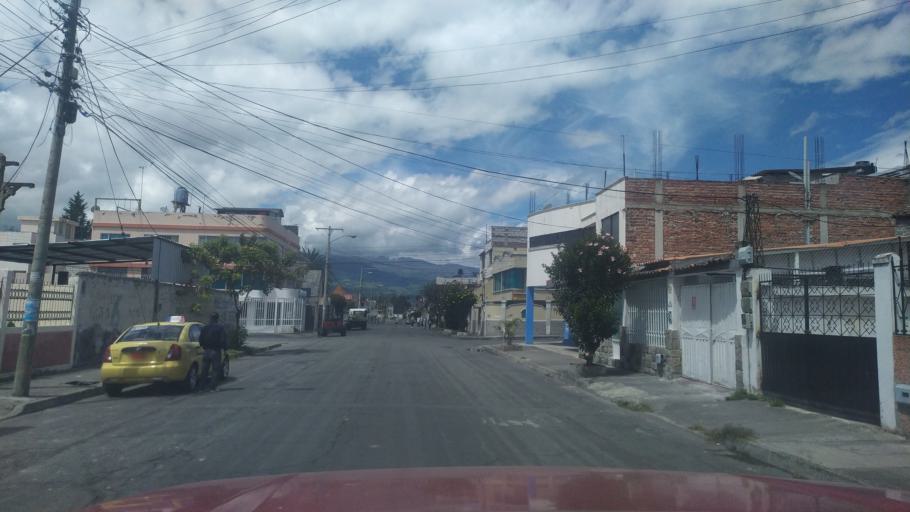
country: EC
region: Chimborazo
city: Riobamba
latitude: -1.6720
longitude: -78.6419
